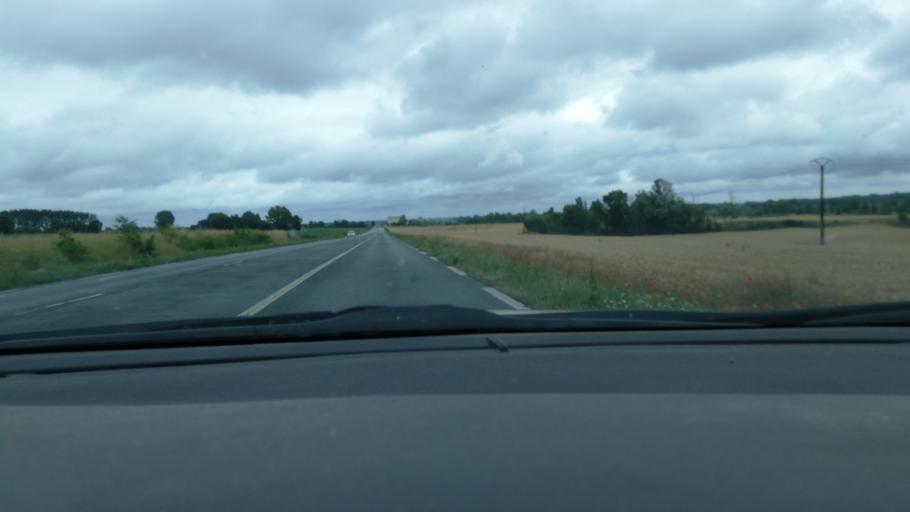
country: FR
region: Poitou-Charentes
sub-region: Departement de la Vienne
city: Naintre
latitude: 46.7400
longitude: 0.4676
